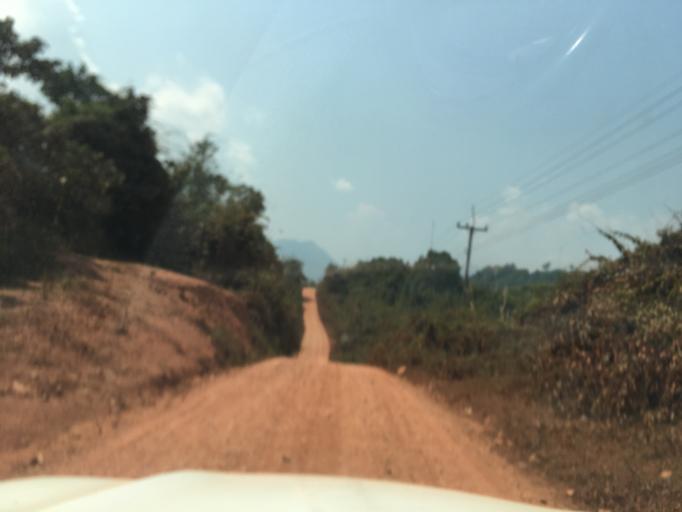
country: LA
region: Bolikhamxai
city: Bolikhan
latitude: 18.7495
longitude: 103.6022
